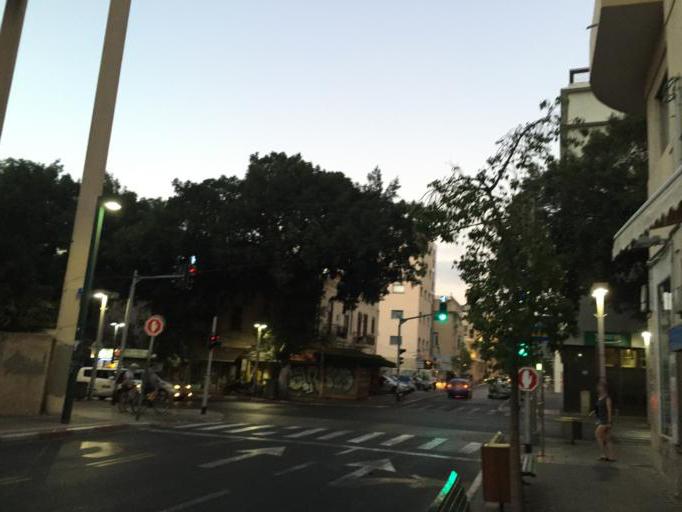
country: IL
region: Tel Aviv
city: Tel Aviv
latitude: 32.0641
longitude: 34.7724
